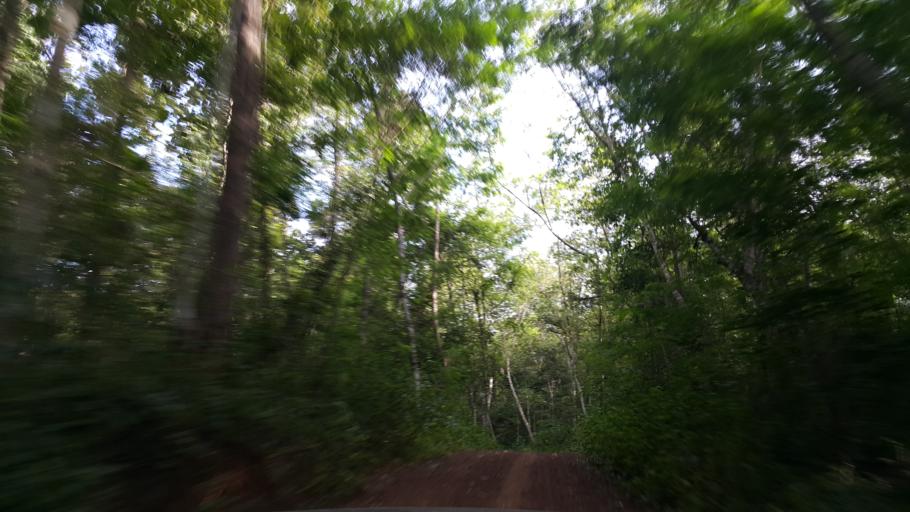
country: TH
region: Chiang Mai
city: Mae On
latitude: 18.8790
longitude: 99.2123
